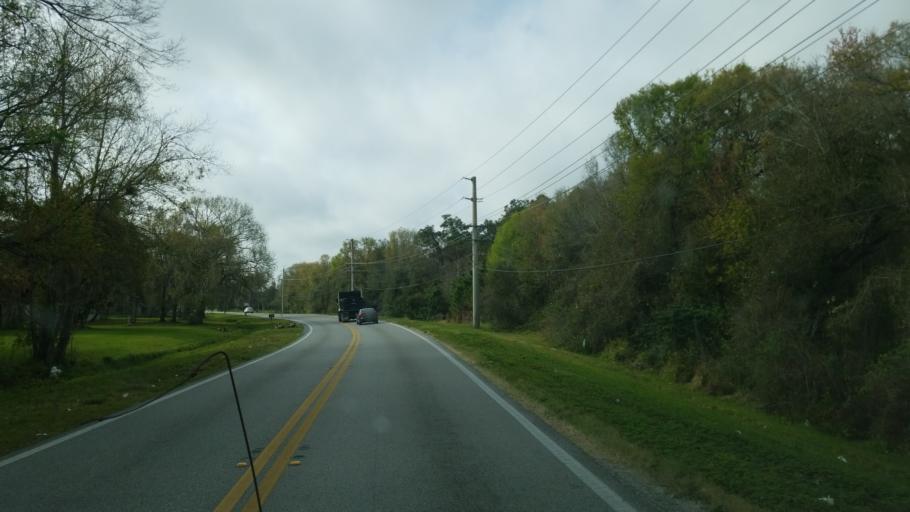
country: US
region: Florida
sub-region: Polk County
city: Winston
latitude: 28.0391
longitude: -82.0193
